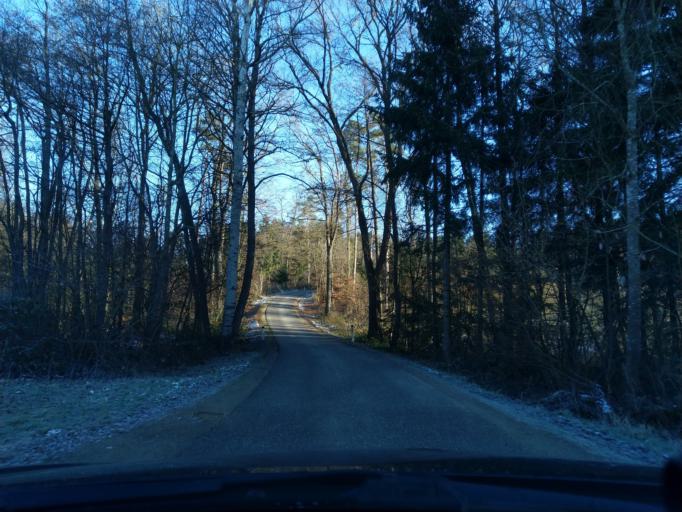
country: AT
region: Upper Austria
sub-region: Politischer Bezirk Urfahr-Umgebung
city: Engerwitzdorf
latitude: 48.3737
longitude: 14.4876
